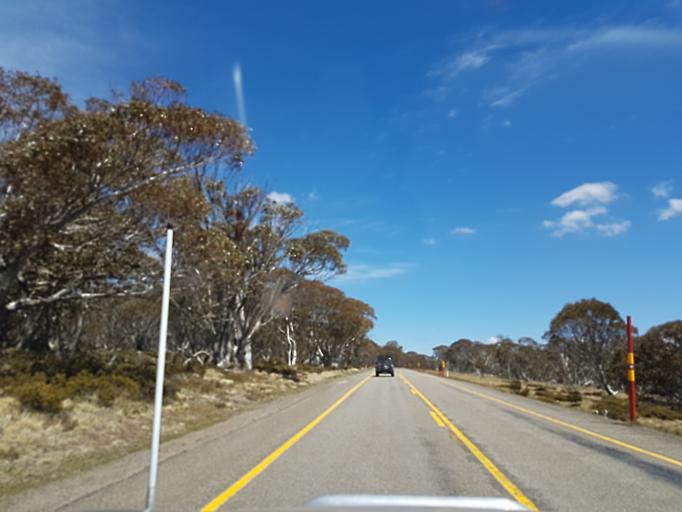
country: AU
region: Victoria
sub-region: Alpine
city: Mount Beauty
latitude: -37.0222
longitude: 147.2547
